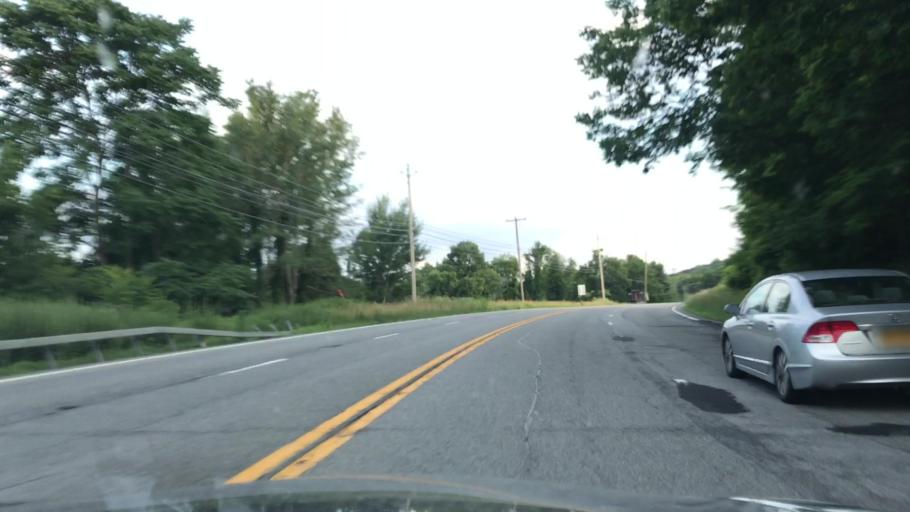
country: US
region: New York
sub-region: Orange County
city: Harriman
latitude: 41.2985
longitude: -74.1438
